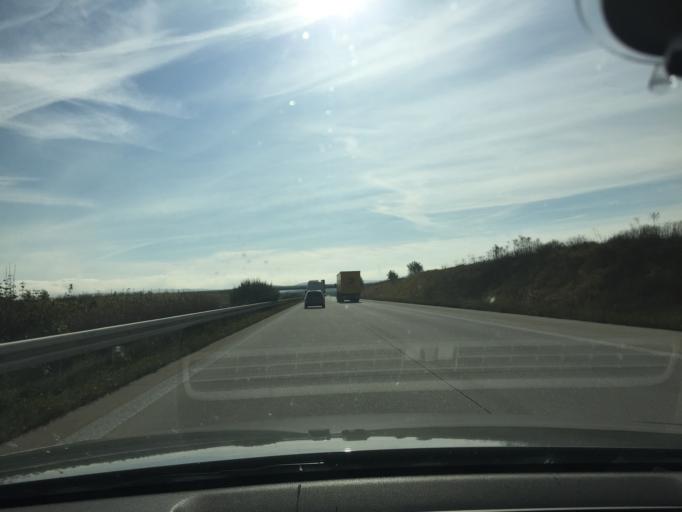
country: DE
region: Saxony
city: Dohma
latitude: 50.9124
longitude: 13.8928
